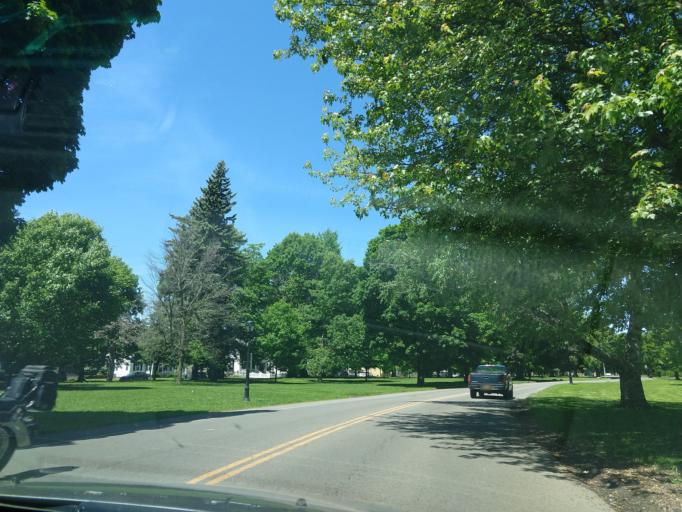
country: US
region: New York
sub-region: Erie County
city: West Seneca
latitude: 42.8454
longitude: -78.8077
